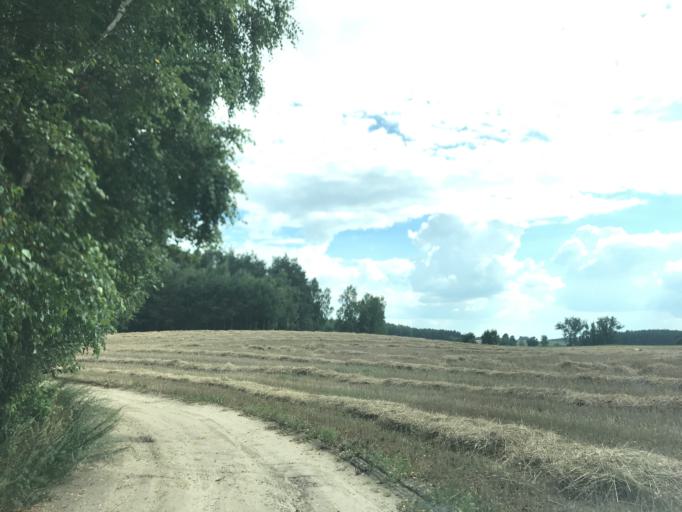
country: PL
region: Kujawsko-Pomorskie
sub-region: Powiat brodnicki
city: Brzozie
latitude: 53.3249
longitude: 19.6871
